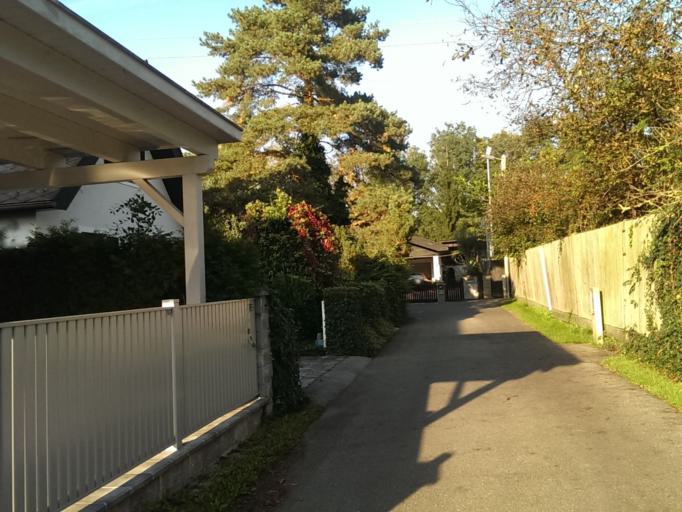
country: AT
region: Styria
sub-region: Graz Stadt
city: Goesting
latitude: 47.1010
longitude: 15.4076
